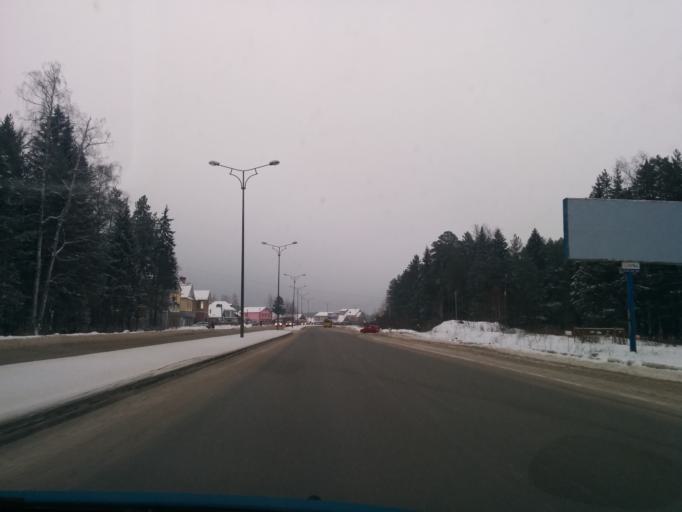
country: RU
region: Perm
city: Kondratovo
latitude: 58.0241
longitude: 55.9962
